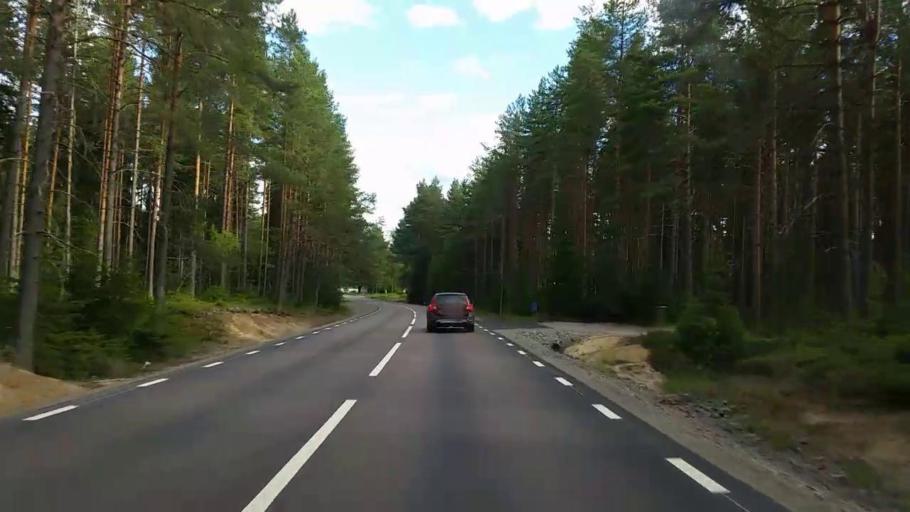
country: SE
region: Gaevleborg
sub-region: Ljusdals Kommun
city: Ljusdal
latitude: 61.8625
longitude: 15.9835
